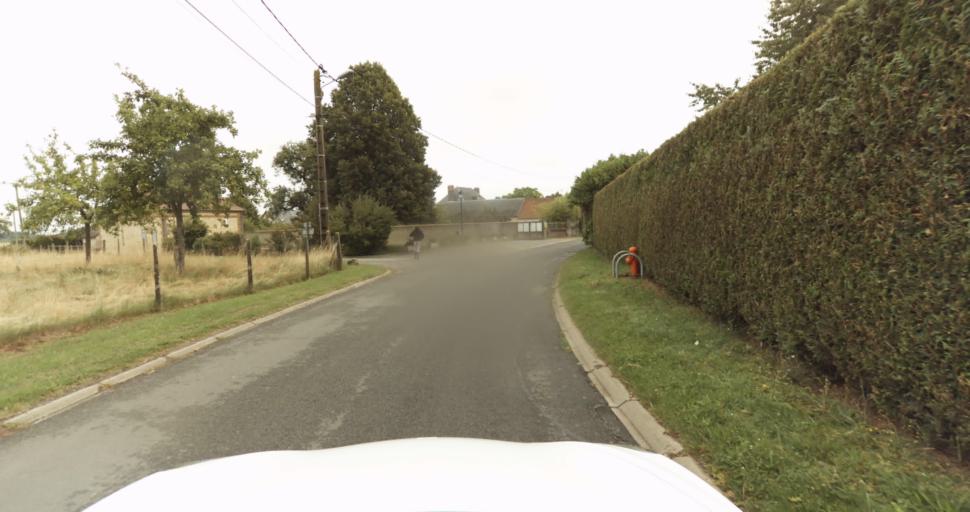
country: FR
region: Haute-Normandie
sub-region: Departement de l'Eure
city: Aviron
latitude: 49.0695
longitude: 1.1000
